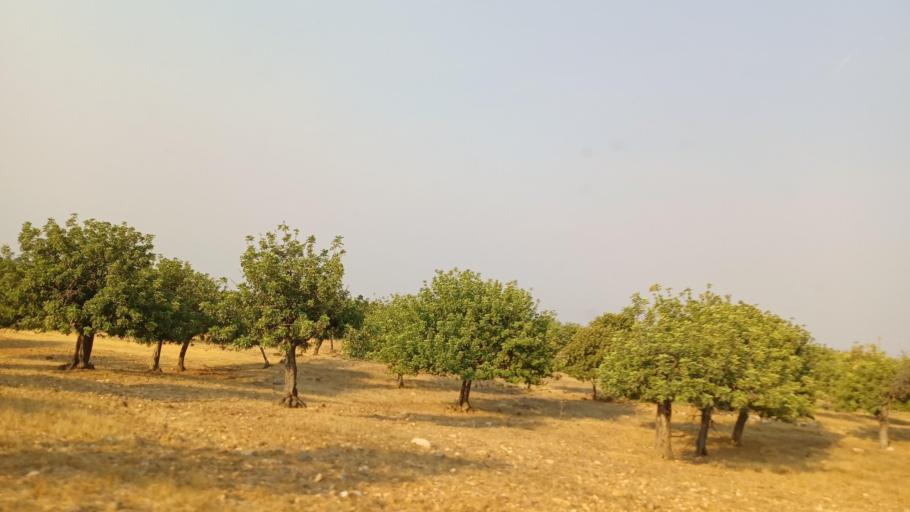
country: CY
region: Limassol
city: Pissouri
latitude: 34.7010
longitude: 32.6571
